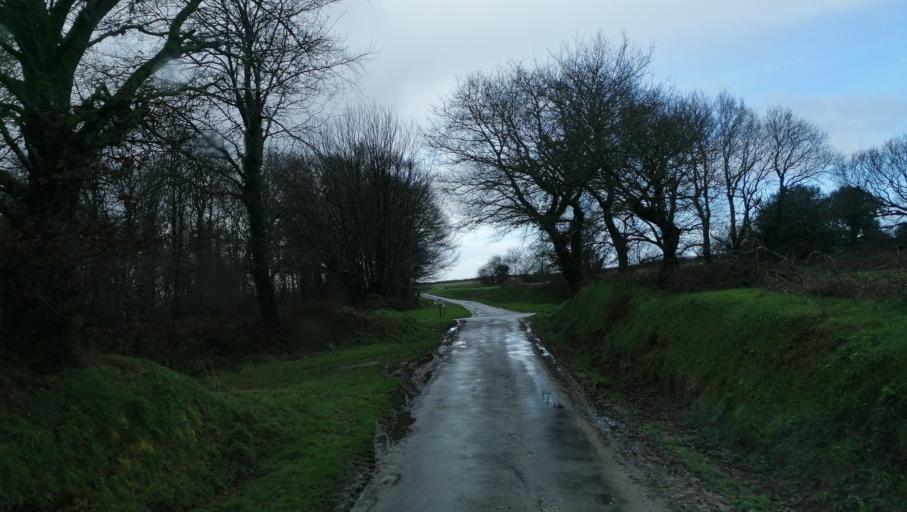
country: FR
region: Brittany
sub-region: Departement des Cotes-d'Armor
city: Plouagat
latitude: 48.4867
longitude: -2.9879
